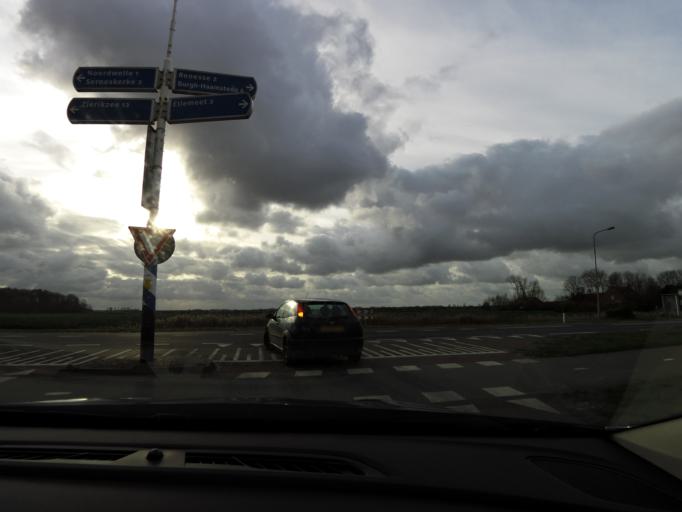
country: NL
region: Zeeland
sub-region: Schouwen-Duiveland
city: Renesse
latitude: 51.7239
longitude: 3.7908
